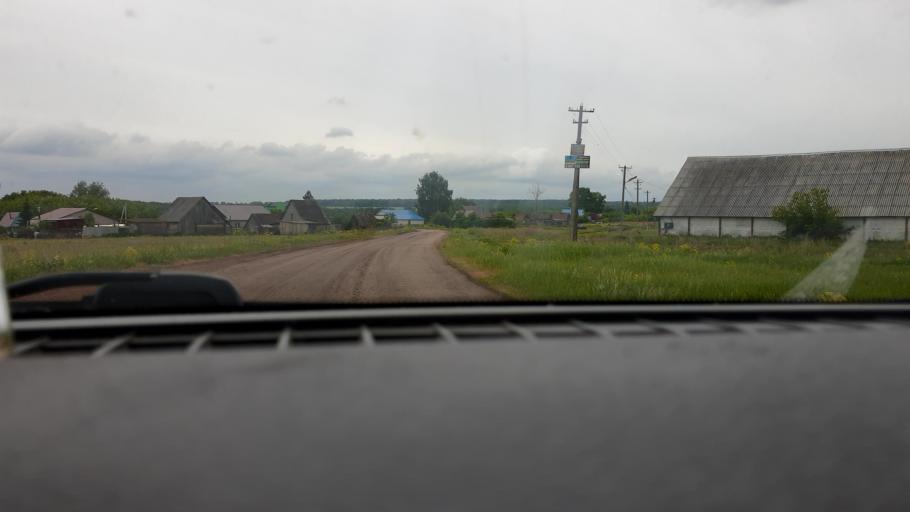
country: RU
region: Bashkortostan
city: Dmitriyevka
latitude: 54.7266
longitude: 55.4992
